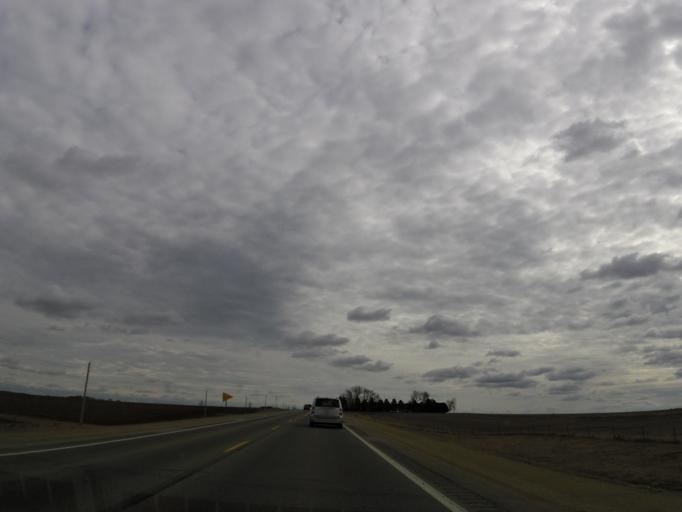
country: US
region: Iowa
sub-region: Chickasaw County
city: New Hampton
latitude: 43.1622
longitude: -92.2989
